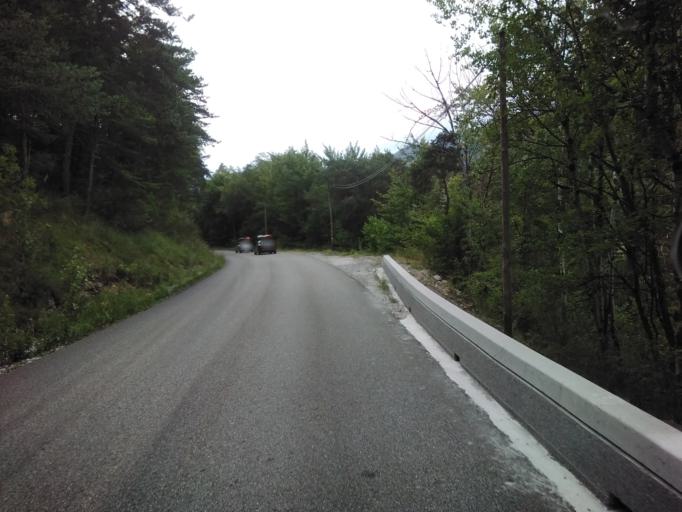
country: FR
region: Provence-Alpes-Cote d'Azur
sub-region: Departement des Alpes-de-Haute-Provence
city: Seyne-les-Alpes
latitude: 44.4488
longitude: 6.3968
